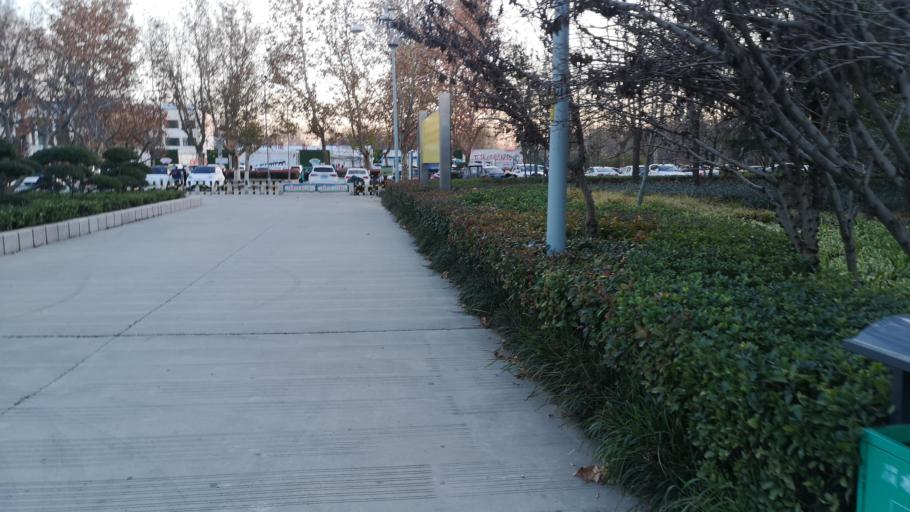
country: CN
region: Henan Sheng
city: Puyang
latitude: 35.7630
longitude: 115.0024
